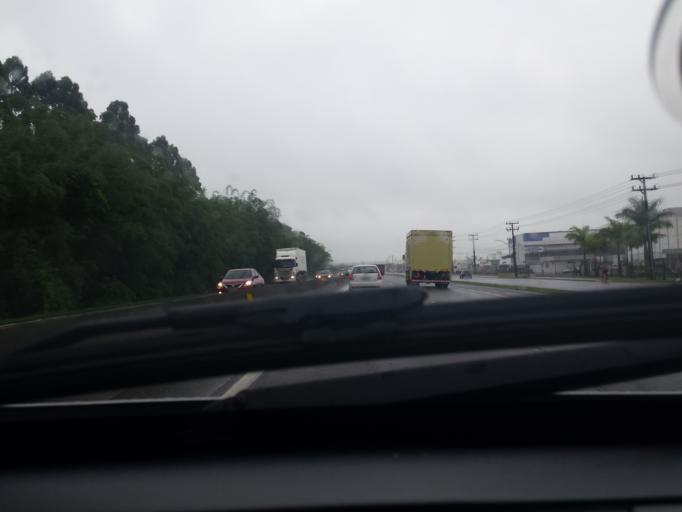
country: BR
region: Santa Catarina
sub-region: Itajai
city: Itajai
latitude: -26.9271
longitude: -48.7059
